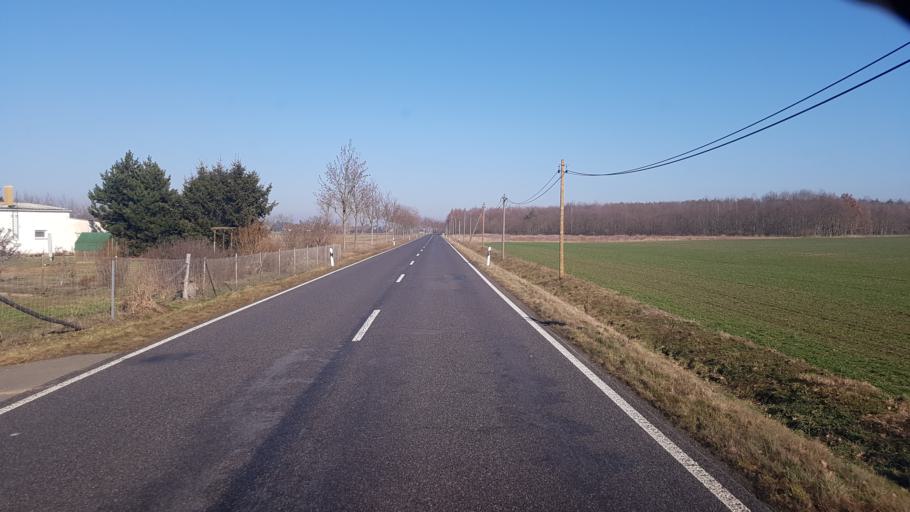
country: DE
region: Brandenburg
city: Ihlow
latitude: 51.8152
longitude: 13.3380
